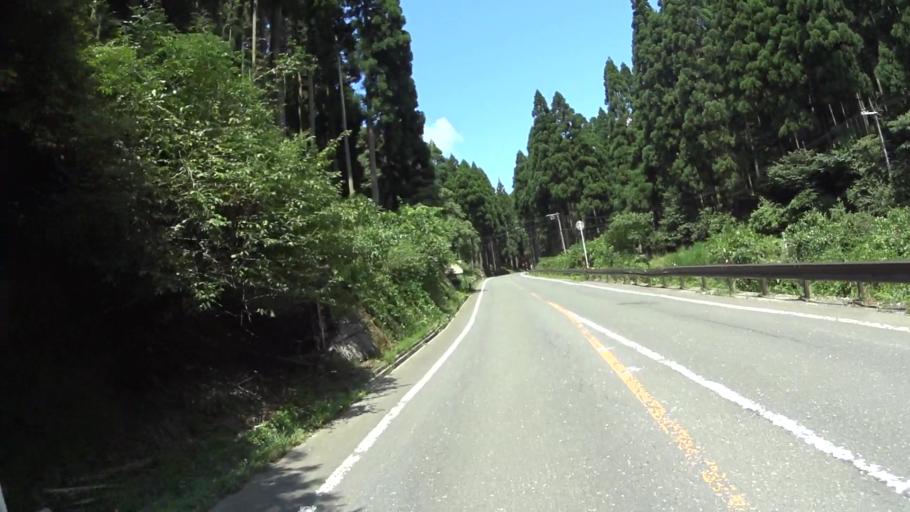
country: JP
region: Shiga Prefecture
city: Kitahama
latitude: 35.3682
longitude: 135.9198
